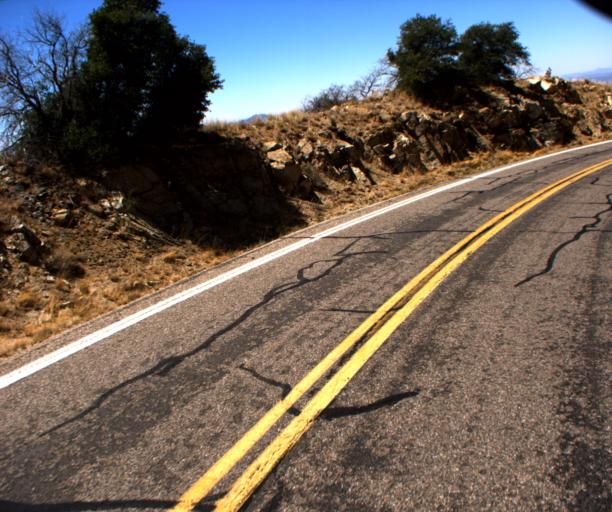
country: US
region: Arizona
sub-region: Pima County
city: Sells
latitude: 31.9613
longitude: -111.6252
